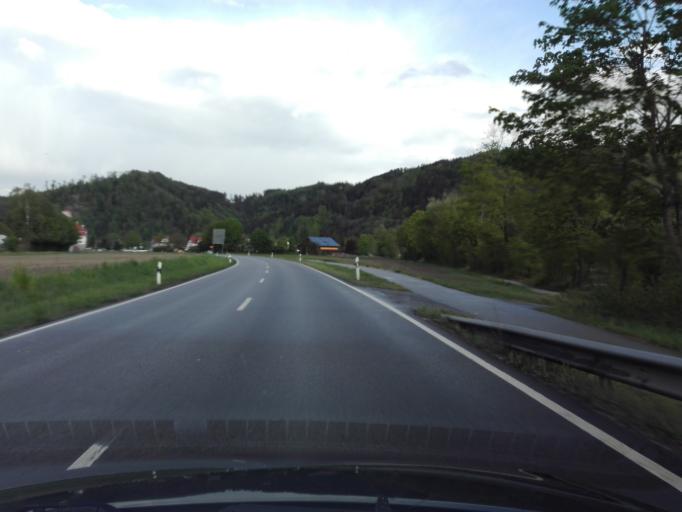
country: DE
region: Bavaria
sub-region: Lower Bavaria
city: Thyrnau
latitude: 48.5629
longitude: 13.5694
